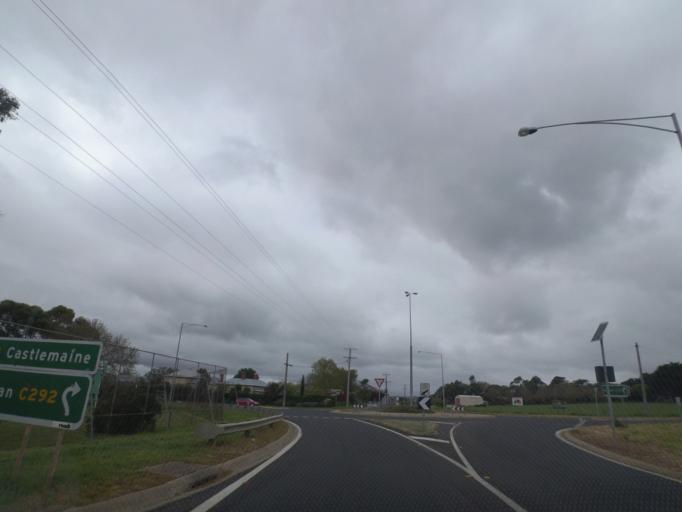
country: AU
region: Victoria
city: Brown Hill
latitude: -37.4122
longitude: 143.9845
